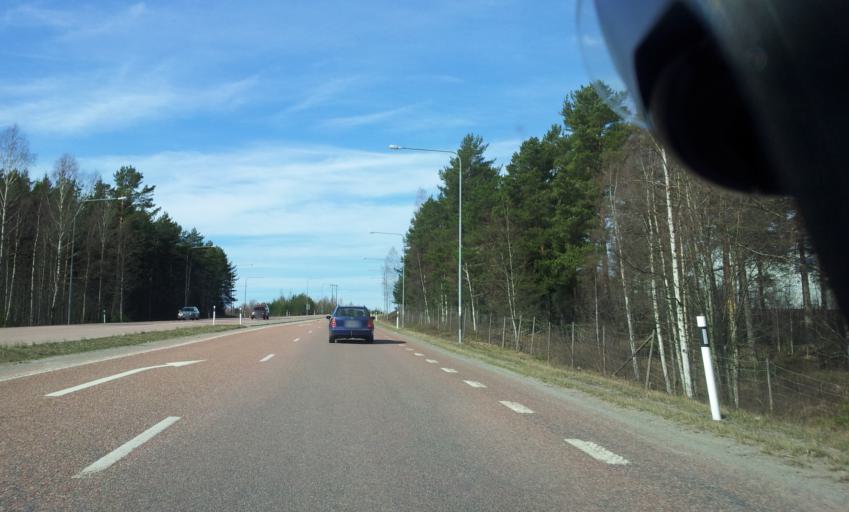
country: SE
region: Gaevleborg
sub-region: Hudiksvalls Kommun
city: Hudiksvall
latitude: 61.7139
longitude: 17.0817
